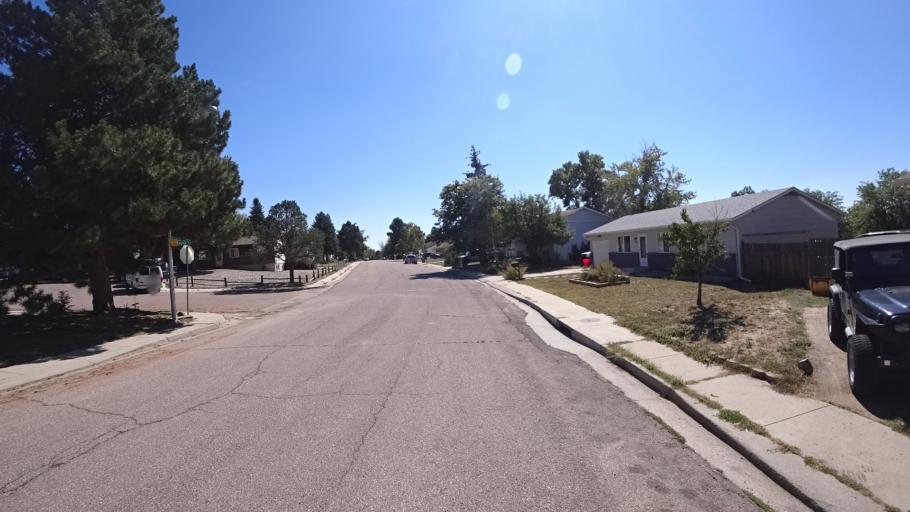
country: US
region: Colorado
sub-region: El Paso County
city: Cimarron Hills
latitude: 38.9051
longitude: -104.7696
